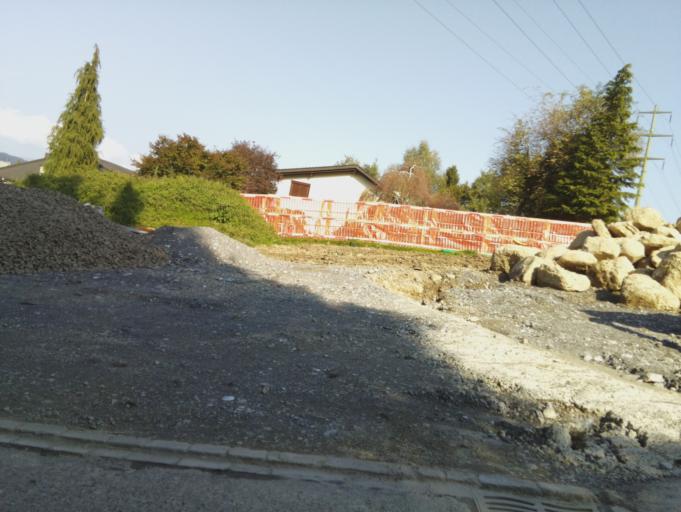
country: CH
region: Schwyz
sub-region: Bezirk March
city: Lachen
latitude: 47.1744
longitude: 8.8778
